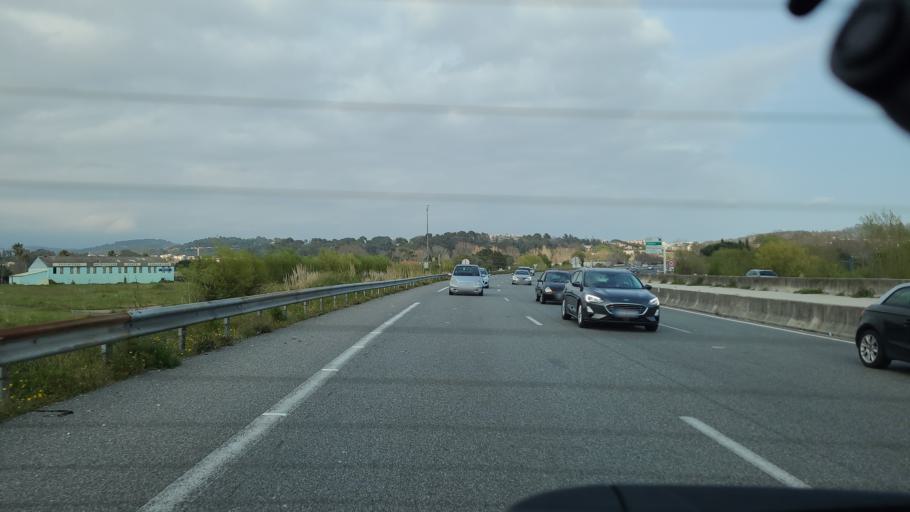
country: FR
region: Provence-Alpes-Cote d'Azur
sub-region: Departement des Alpes-Maritimes
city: Mandelieu-la-Napoule
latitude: 43.5571
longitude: 6.9477
